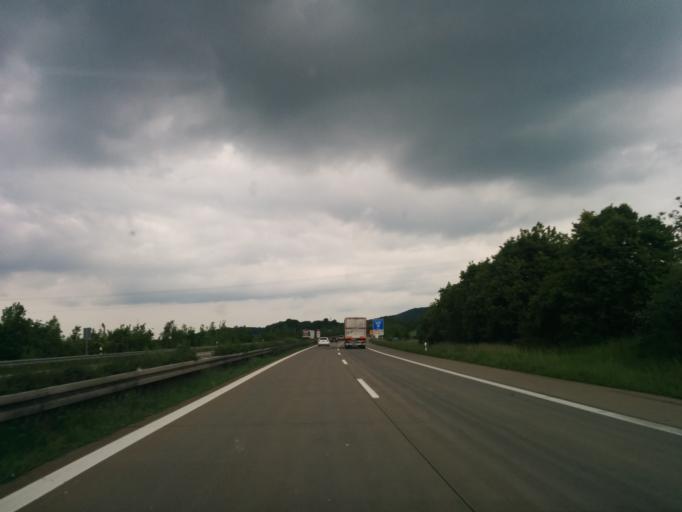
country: DE
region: Bavaria
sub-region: Regierungsbezirk Mittelfranken
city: Steinsfeld
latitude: 49.4152
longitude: 10.2478
